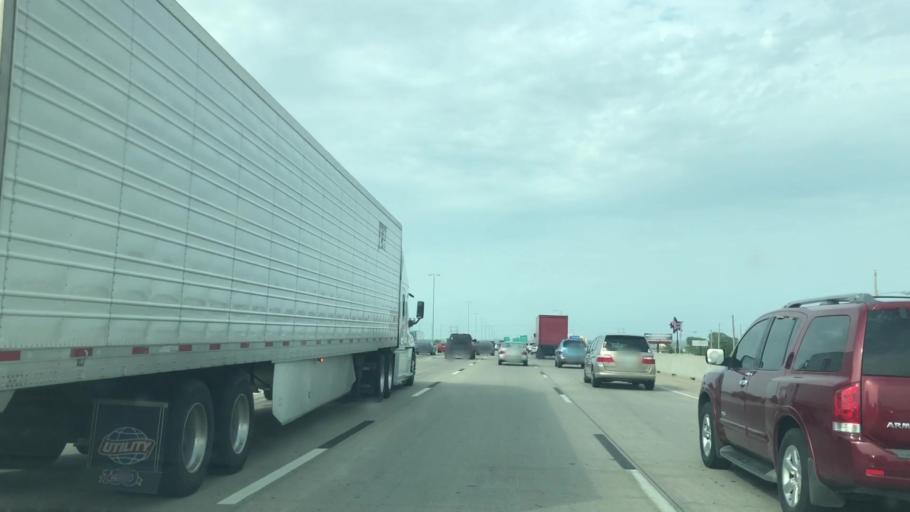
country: US
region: Oklahoma
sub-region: Tulsa County
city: Tulsa
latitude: 36.1066
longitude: -95.9065
